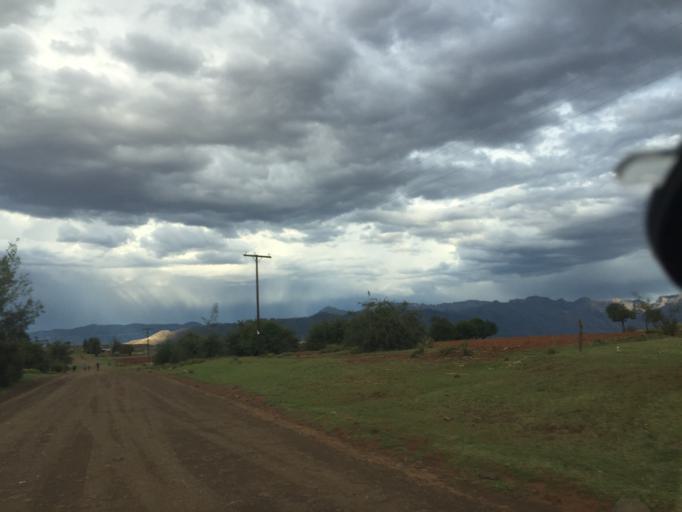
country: LS
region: Leribe
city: Leribe
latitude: -29.1547
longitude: 28.0371
